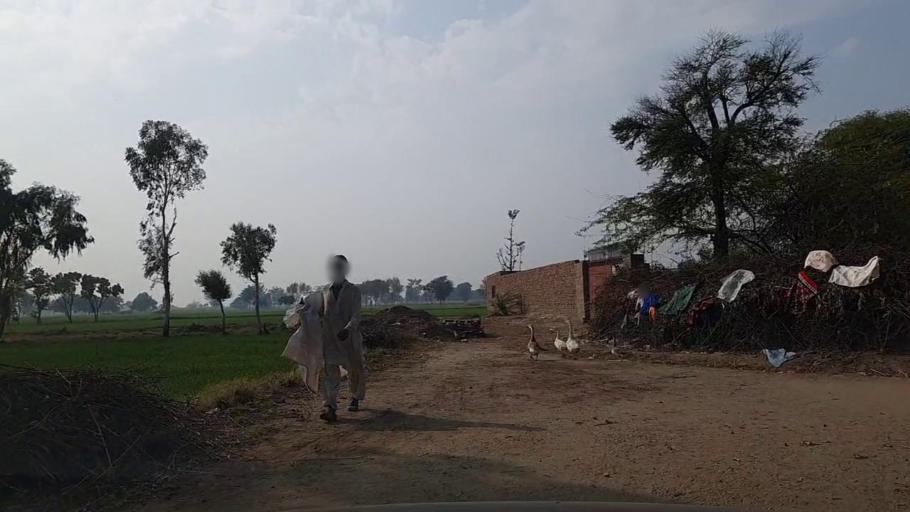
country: PK
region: Sindh
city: Nawabshah
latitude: 26.2757
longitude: 68.4390
